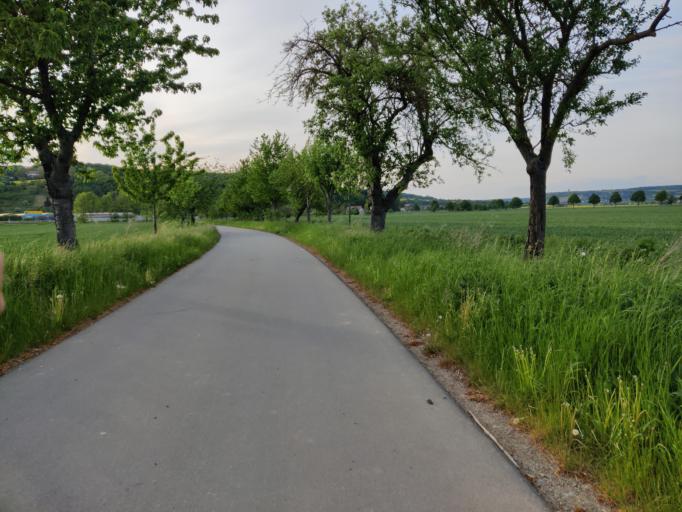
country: DE
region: Saxony-Anhalt
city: Naumburg
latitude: 51.1701
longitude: 11.7852
